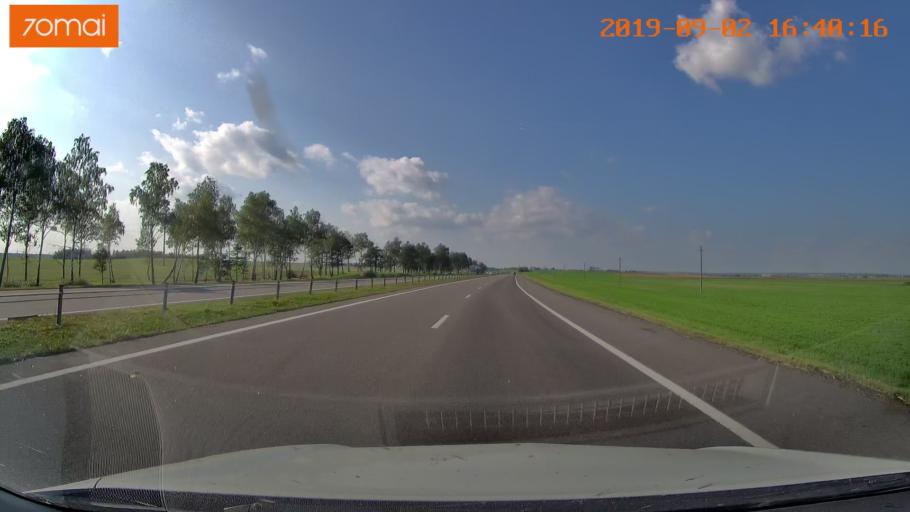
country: BY
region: Minsk
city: Luhavaya Slabada
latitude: 53.7659
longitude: 27.8649
